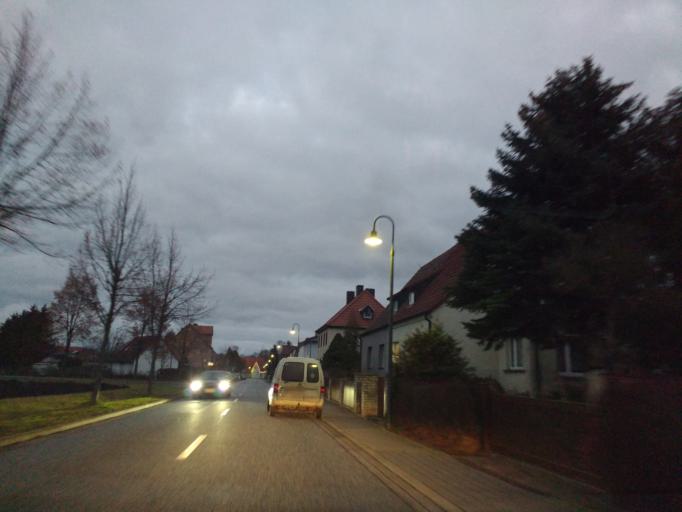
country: DE
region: Saxony-Anhalt
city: Bad Lauchstadt
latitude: 51.3831
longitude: 11.8628
